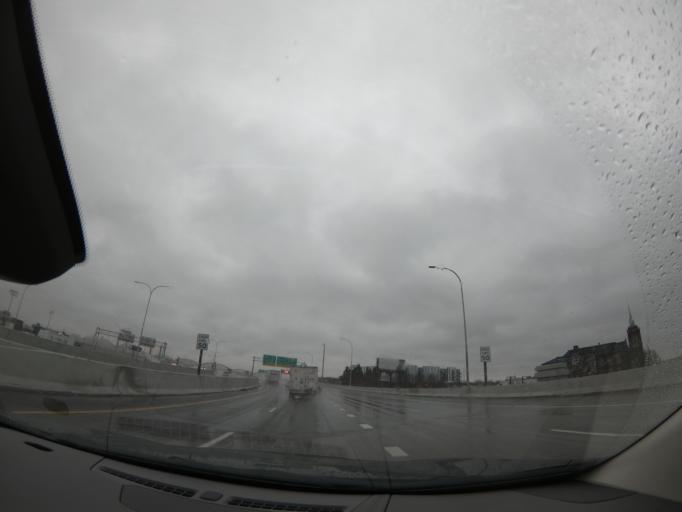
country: US
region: Kentucky
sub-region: Jefferson County
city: Louisville
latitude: 38.2538
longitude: -85.7429
